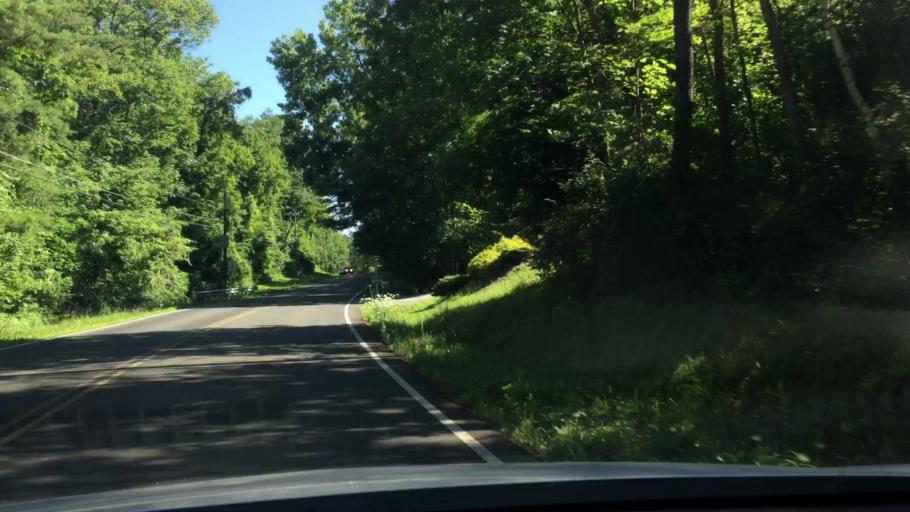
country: US
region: Massachusetts
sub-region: Berkshire County
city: Richmond
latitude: 42.3605
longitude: -73.3535
